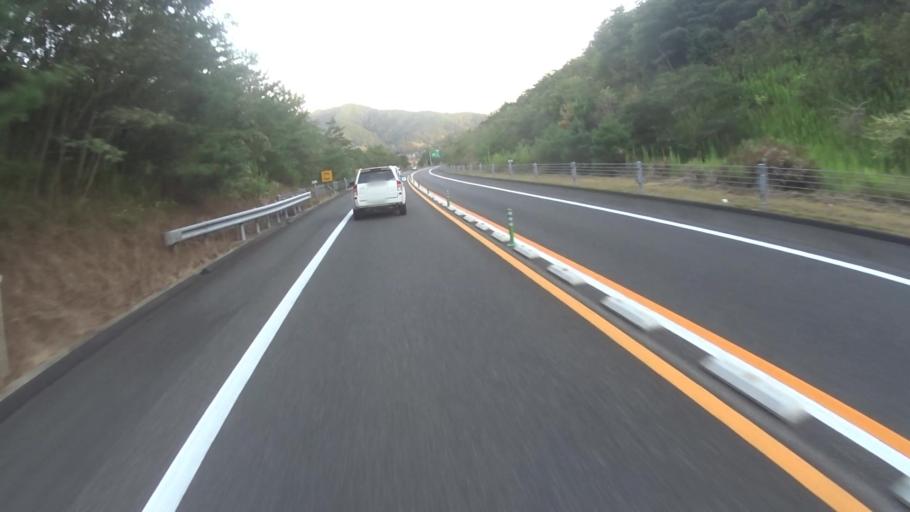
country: JP
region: Kyoto
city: Ayabe
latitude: 35.3645
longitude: 135.2869
